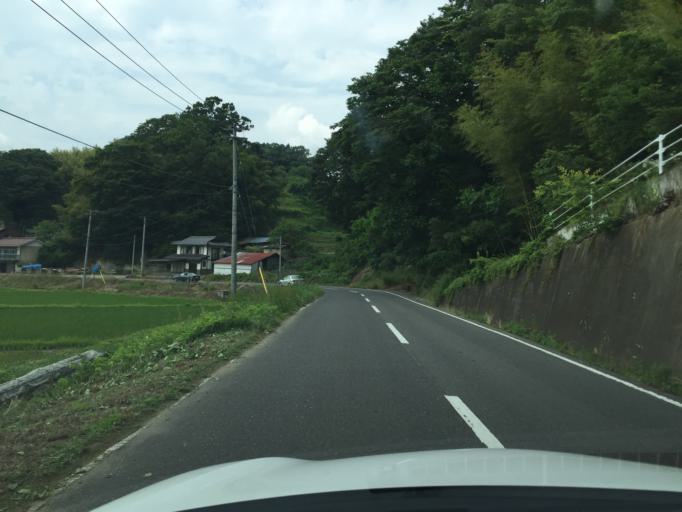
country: JP
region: Fukushima
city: Sukagawa
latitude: 37.2451
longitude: 140.4450
